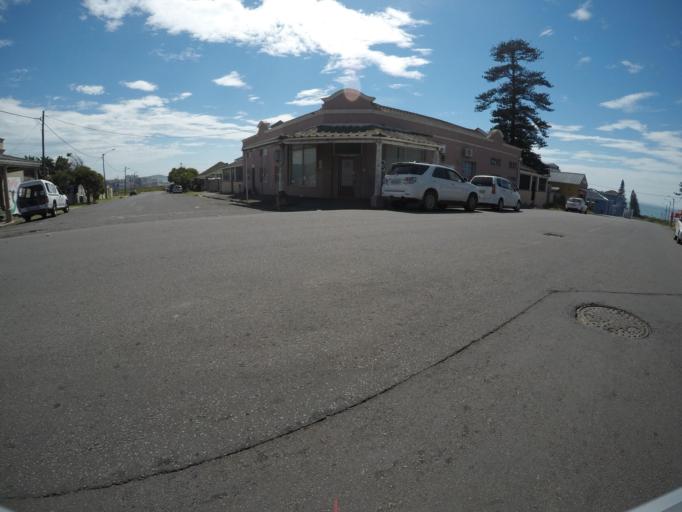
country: ZA
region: Eastern Cape
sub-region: Buffalo City Metropolitan Municipality
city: East London
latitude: -33.0310
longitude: 27.9090
